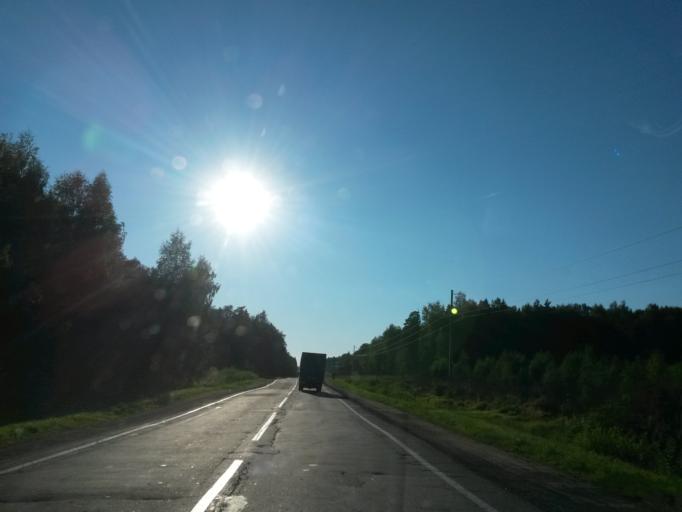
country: RU
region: Jaroslavl
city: Dubki
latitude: 57.2591
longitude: 40.0671
